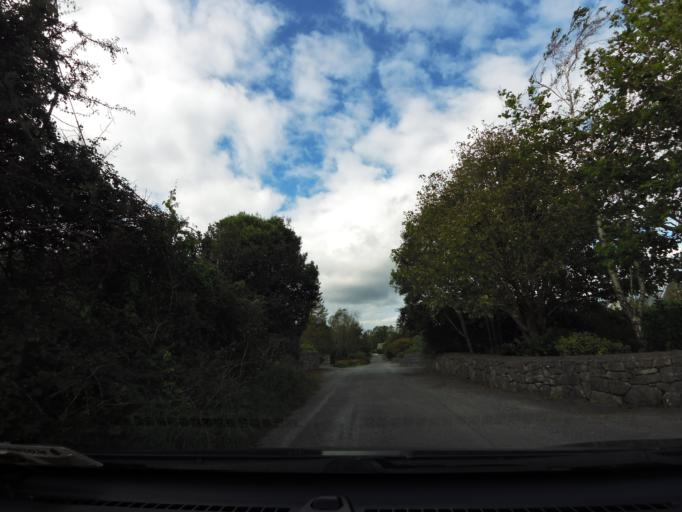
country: IE
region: Connaught
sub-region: County Galway
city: Moycullen
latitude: 53.3566
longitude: -9.1644
